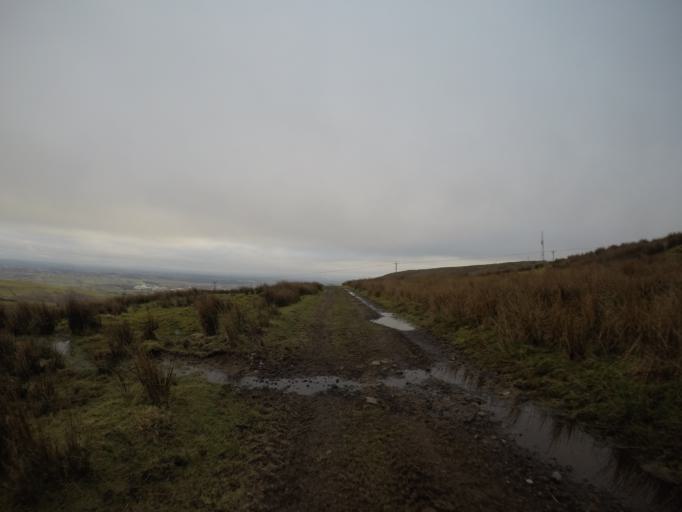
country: GB
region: Scotland
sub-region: North Ayrshire
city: Dalry
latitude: 55.7343
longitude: -4.7680
